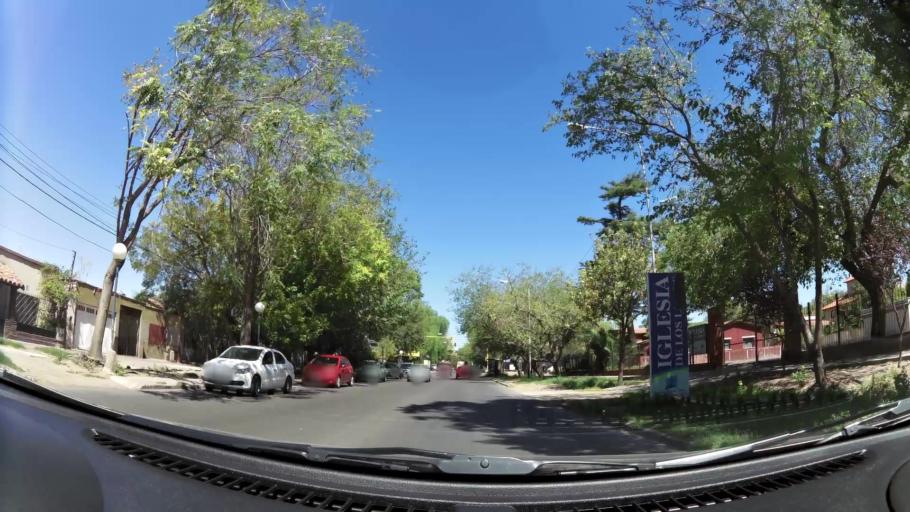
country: AR
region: Mendoza
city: Las Heras
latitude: -32.8511
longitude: -68.8466
